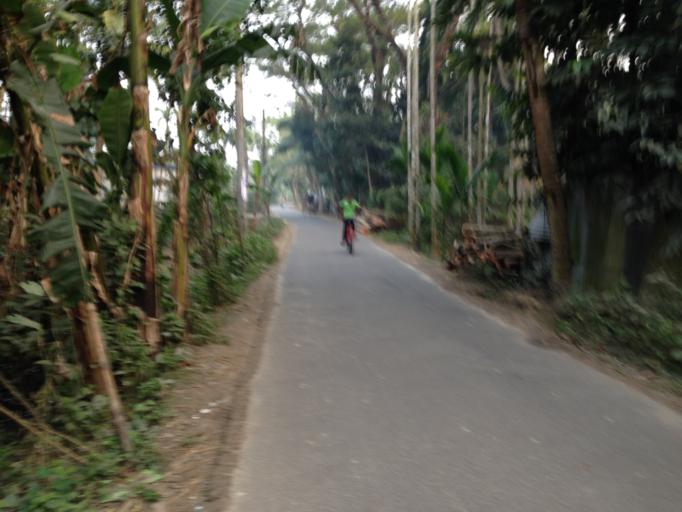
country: BD
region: Chittagong
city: Lakshmipur
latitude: 22.9198
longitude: 90.8400
